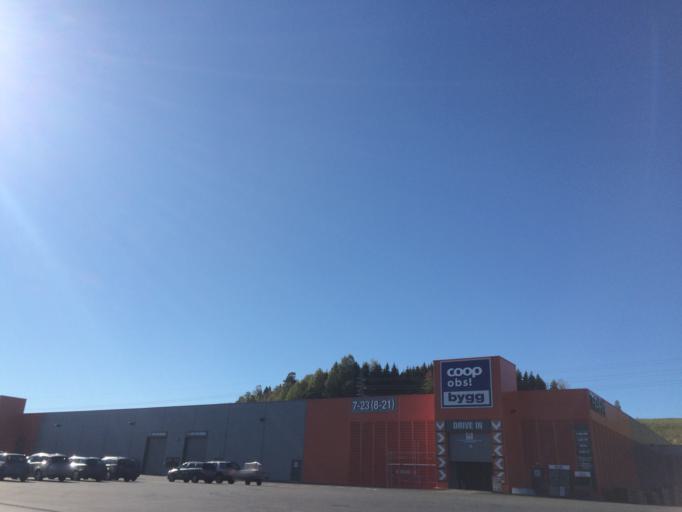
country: NO
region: Akershus
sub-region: Ski
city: Ski
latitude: 59.7263
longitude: 10.7808
